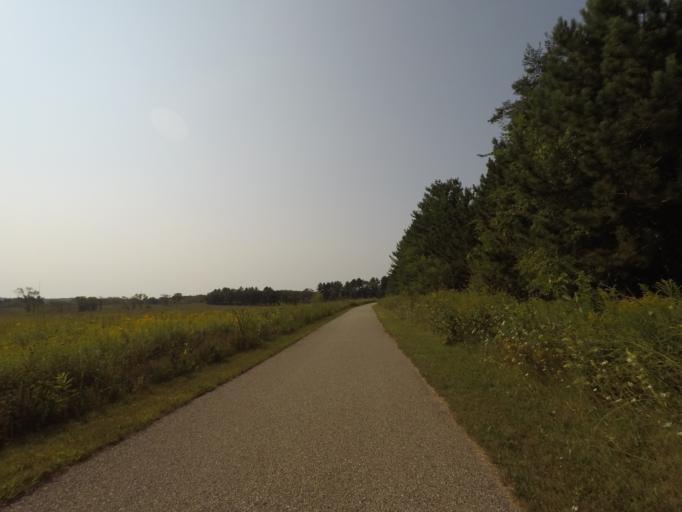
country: US
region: Wisconsin
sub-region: Waukesha County
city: Delafield
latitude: 43.0429
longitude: -88.4139
